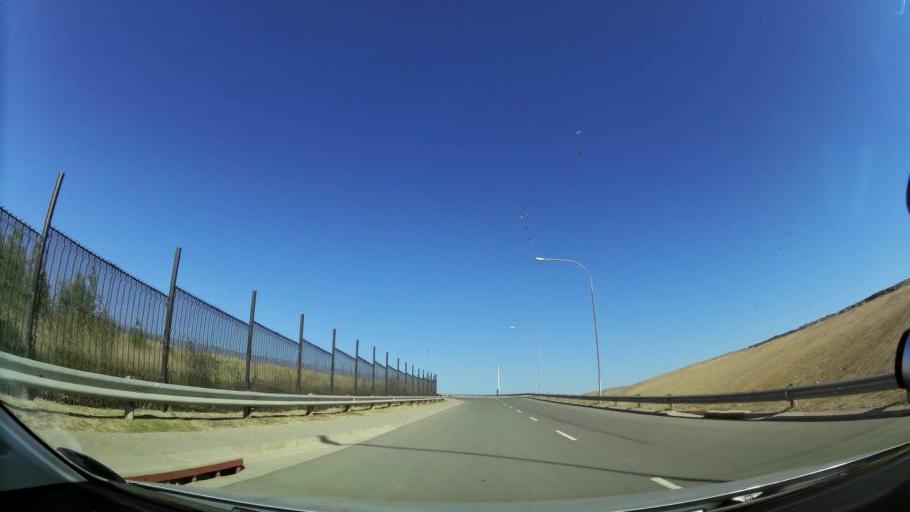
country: ZA
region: Gauteng
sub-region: City of Johannesburg Metropolitan Municipality
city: Modderfontein
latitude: -26.0452
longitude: 28.1707
